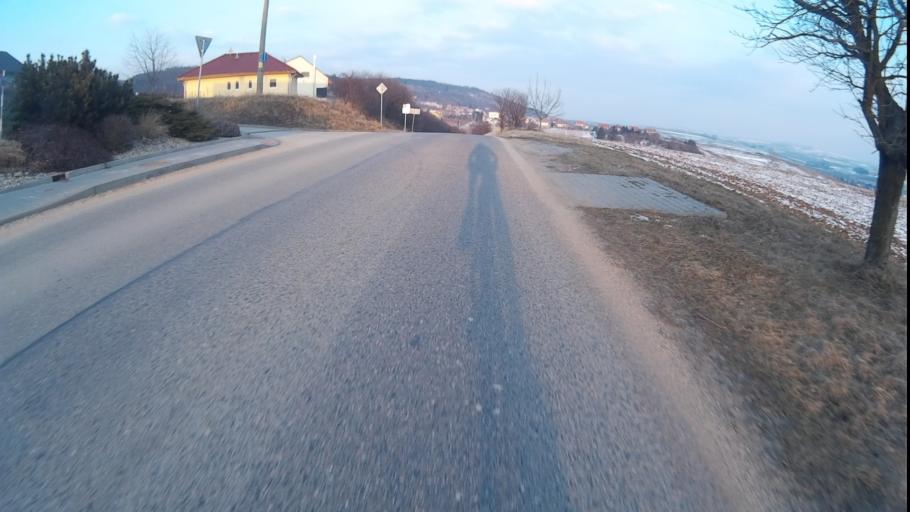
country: CZ
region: South Moravian
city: Pozorice
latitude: 49.2111
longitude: 16.8057
